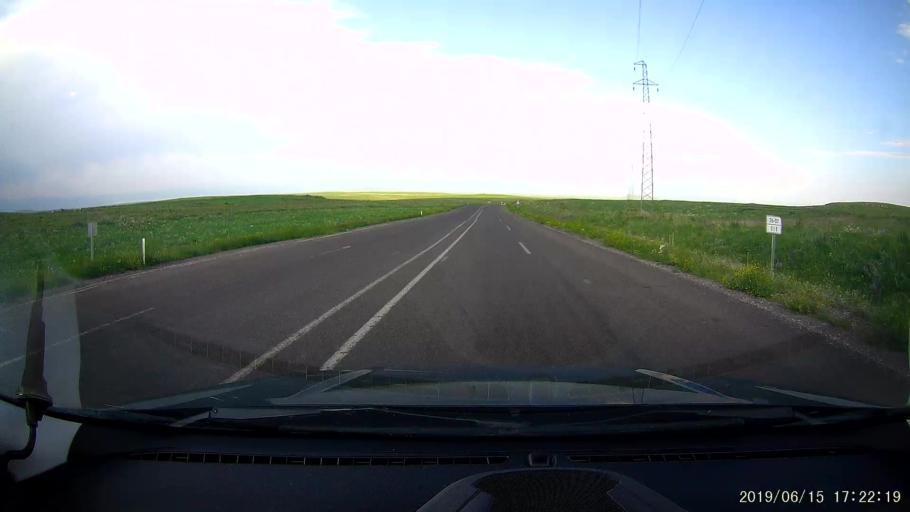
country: TR
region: Kars
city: Basgedikler
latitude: 40.6190
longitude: 43.3413
